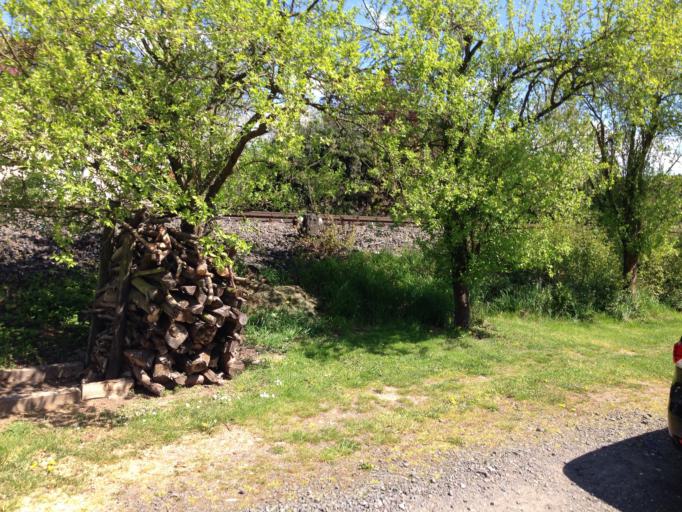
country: DE
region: Hesse
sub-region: Regierungsbezirk Giessen
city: Lich
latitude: 50.5187
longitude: 8.8078
